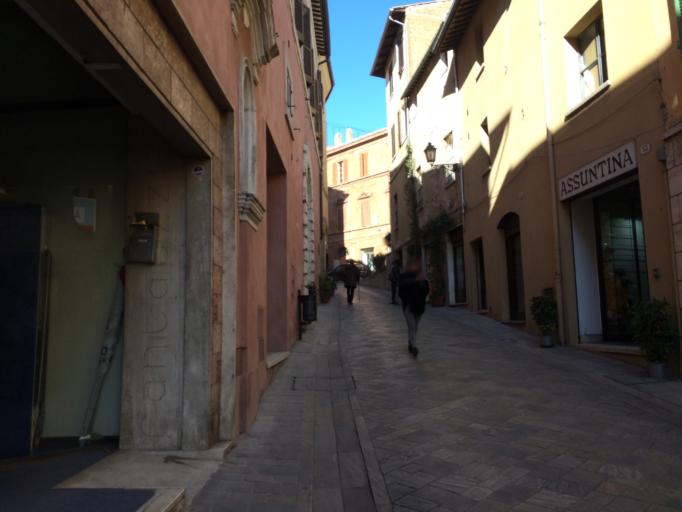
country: IT
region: Umbria
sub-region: Provincia di Terni
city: Amelia
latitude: 42.5546
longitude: 12.4162
